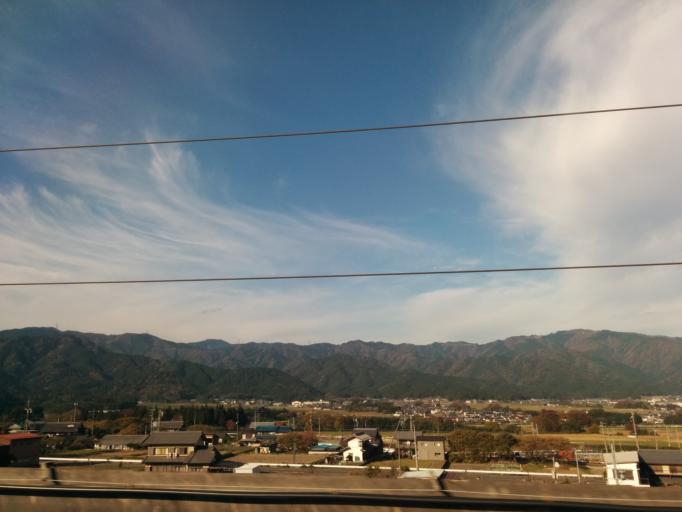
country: JP
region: Gifu
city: Tarui
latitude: 35.3695
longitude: 136.5053
